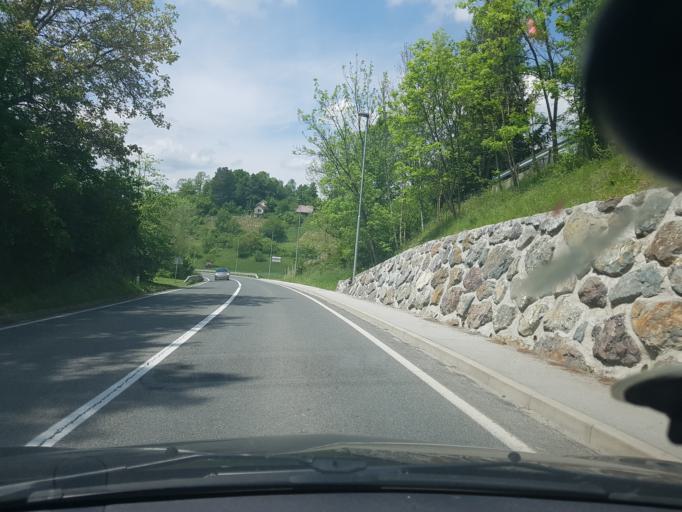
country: SI
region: Rogaska Slatina
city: Rogaska Slatina
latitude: 46.2487
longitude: 15.6446
